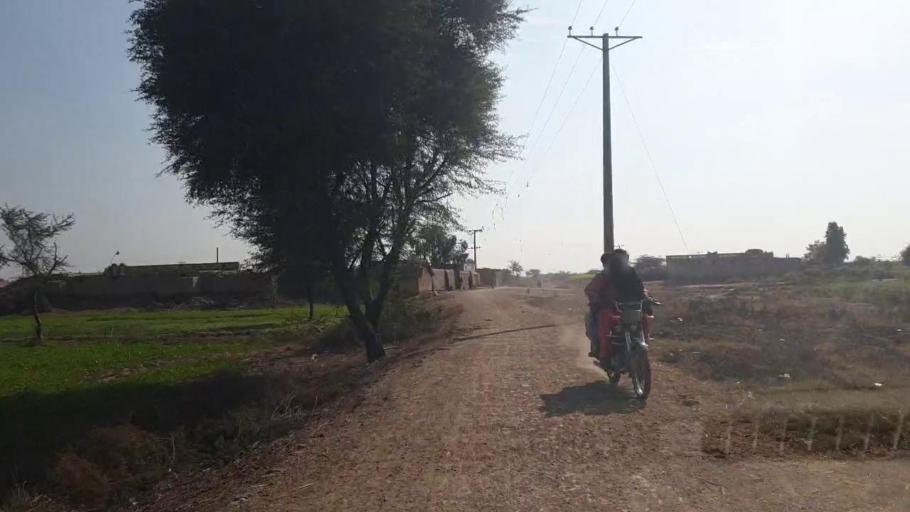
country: PK
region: Sindh
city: Shahdadpur
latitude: 25.9884
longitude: 68.5481
